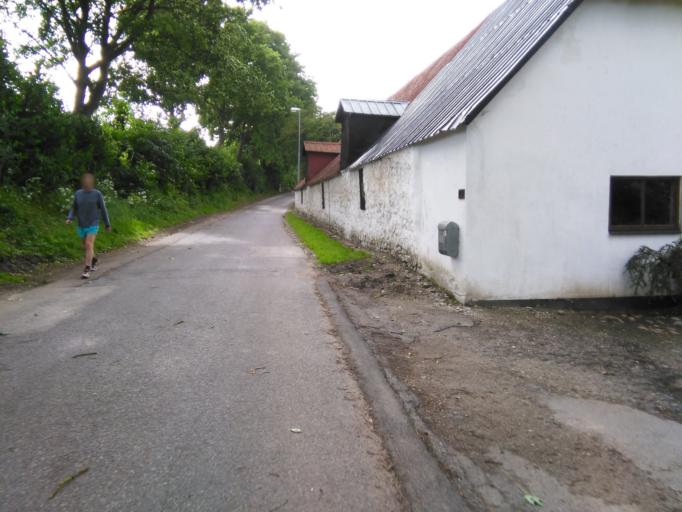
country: DK
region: Central Jutland
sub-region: Arhus Kommune
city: Beder
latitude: 56.0751
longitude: 10.2043
